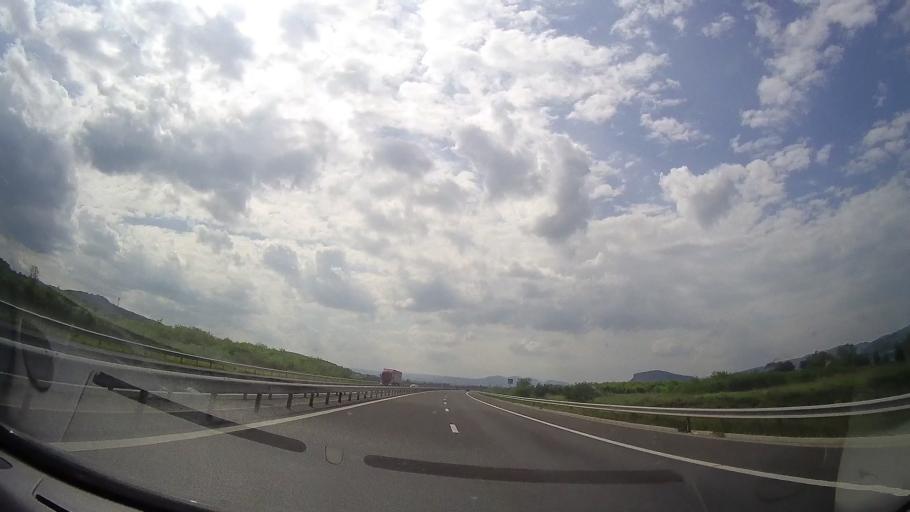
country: RO
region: Hunedoara
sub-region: Comuna Turdas
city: Turdas
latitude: 45.8369
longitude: 23.1037
